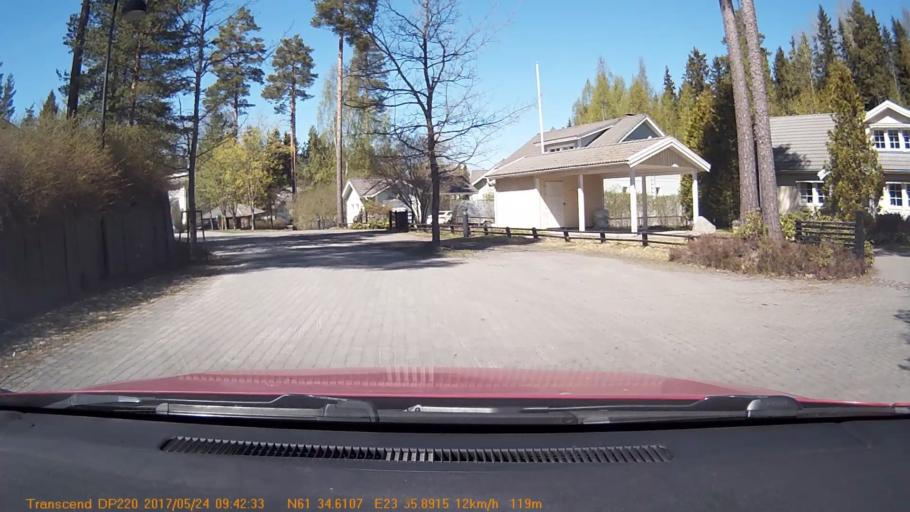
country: FI
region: Pirkanmaa
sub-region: Tampere
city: Yloejaervi
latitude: 61.5769
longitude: 23.5981
